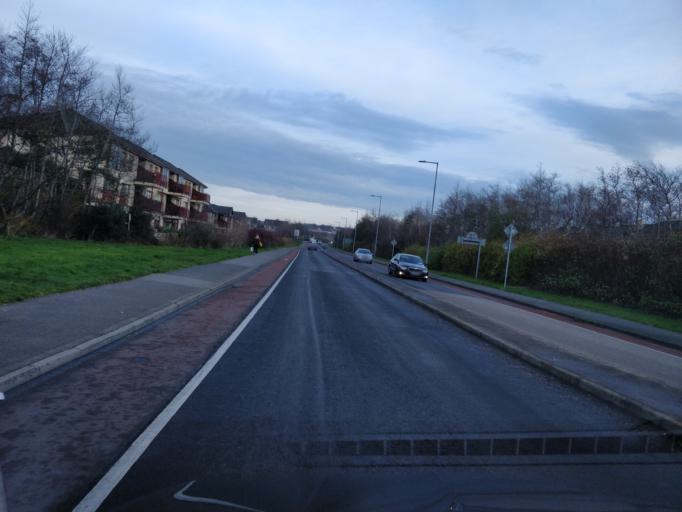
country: IE
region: Connaught
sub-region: County Galway
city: Bearna
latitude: 53.2693
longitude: -9.1064
